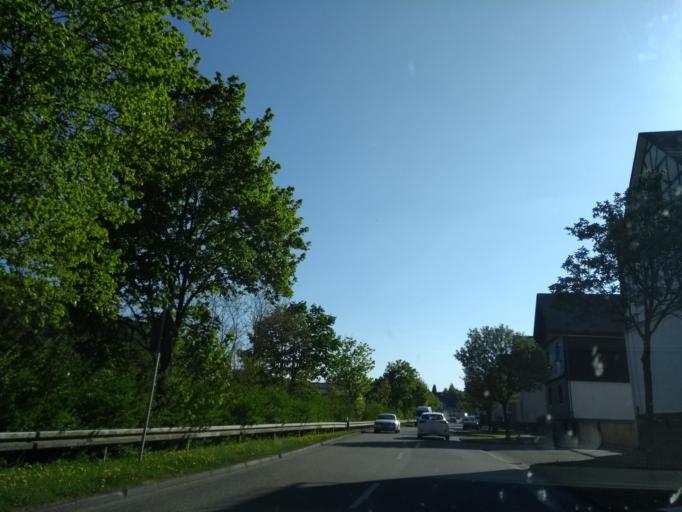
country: DE
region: Hesse
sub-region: Regierungsbezirk Giessen
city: Breidenbach
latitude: 50.8598
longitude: 8.4183
